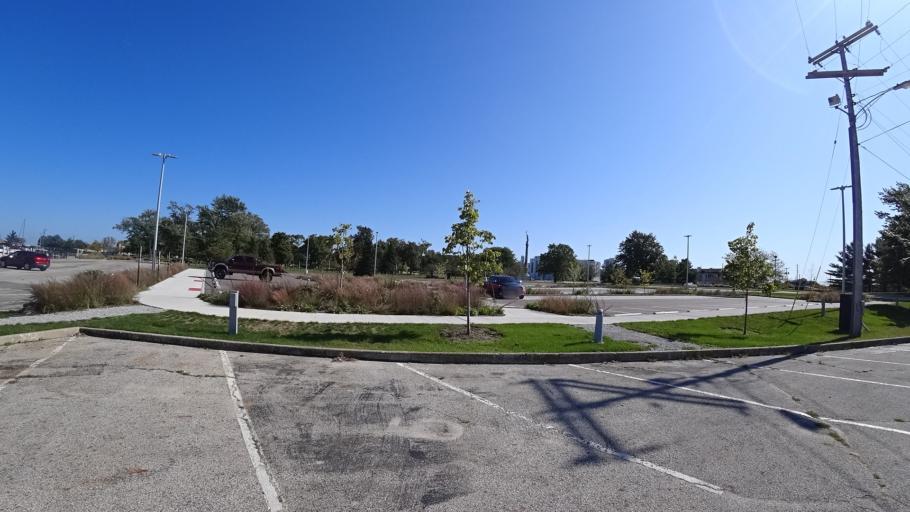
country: US
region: Indiana
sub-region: LaPorte County
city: Michigan City
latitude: 41.7238
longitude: -86.9065
